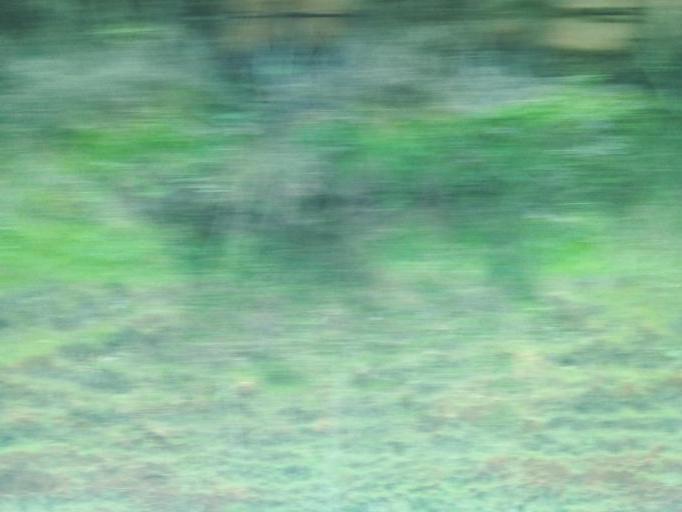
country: BR
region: Minas Gerais
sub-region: Belo Oriente
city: Belo Oriente
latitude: -19.2178
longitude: -42.2990
